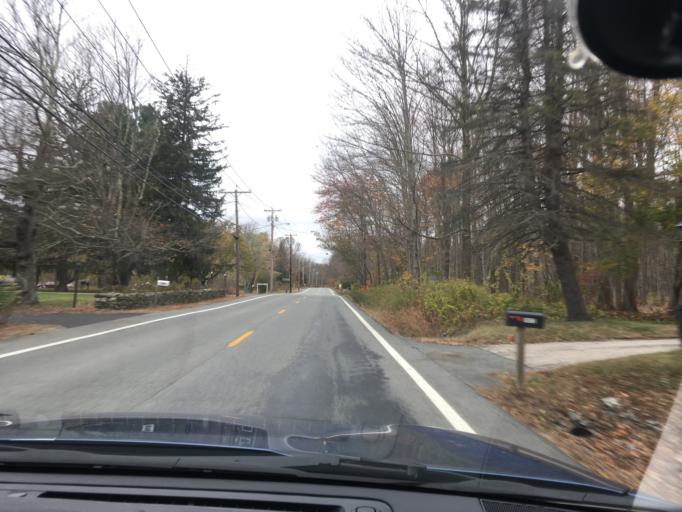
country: US
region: Rhode Island
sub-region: Providence County
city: Chepachet
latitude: 41.8358
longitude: -71.6752
